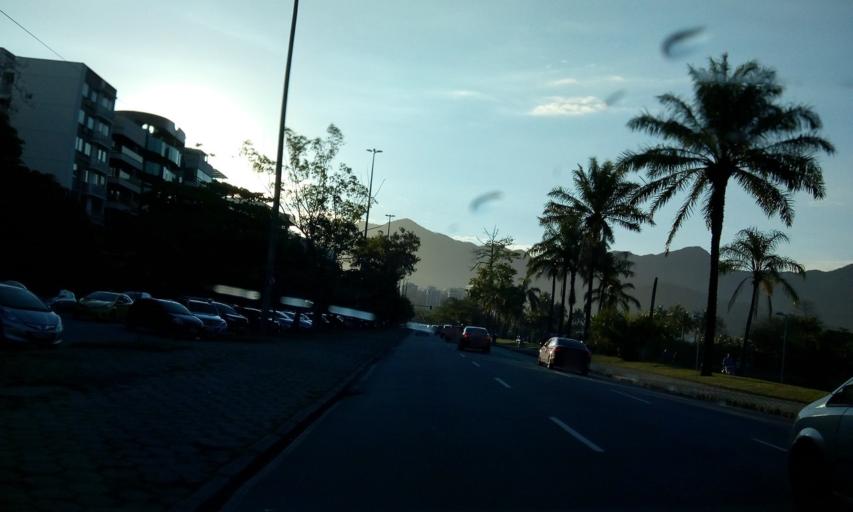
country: BR
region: Rio de Janeiro
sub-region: Rio De Janeiro
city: Rio de Janeiro
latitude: -22.9806
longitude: -43.2093
